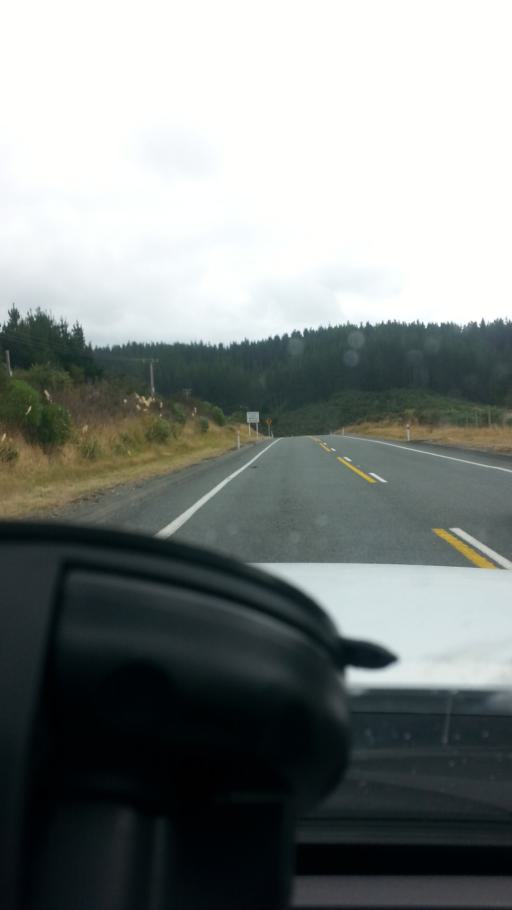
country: NZ
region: Wellington
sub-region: Upper Hutt City
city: Upper Hutt
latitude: -41.0831
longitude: 175.1728
